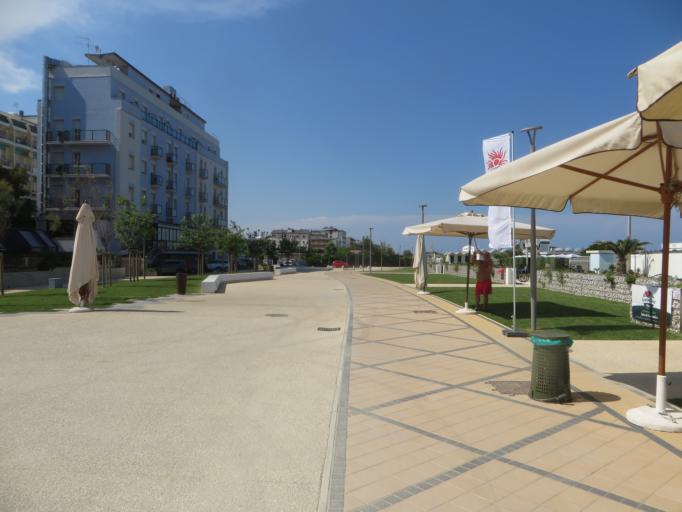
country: IT
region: Emilia-Romagna
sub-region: Provincia di Ravenna
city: Cervia
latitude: 44.2782
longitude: 12.3527
